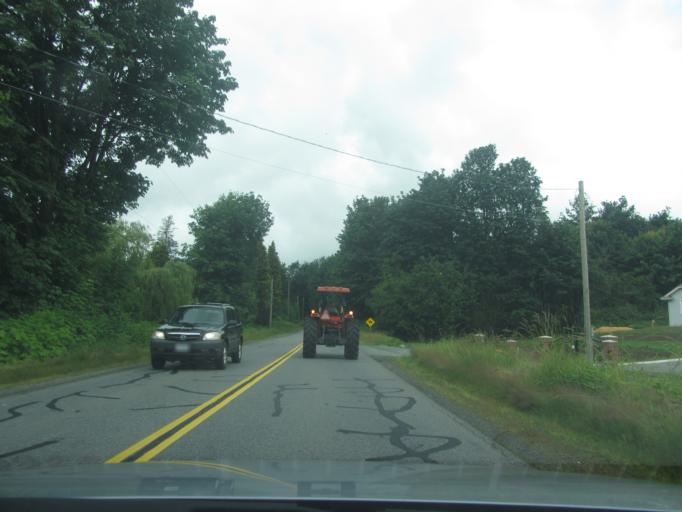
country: CA
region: British Columbia
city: Aldergrove
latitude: 49.1040
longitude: -122.3665
